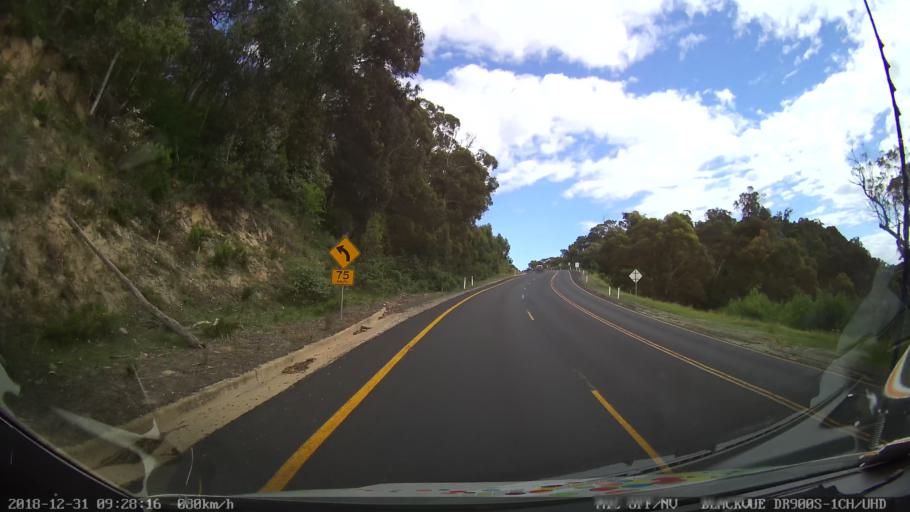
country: AU
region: New South Wales
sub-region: Snowy River
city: Jindabyne
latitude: -36.4575
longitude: 148.4752
